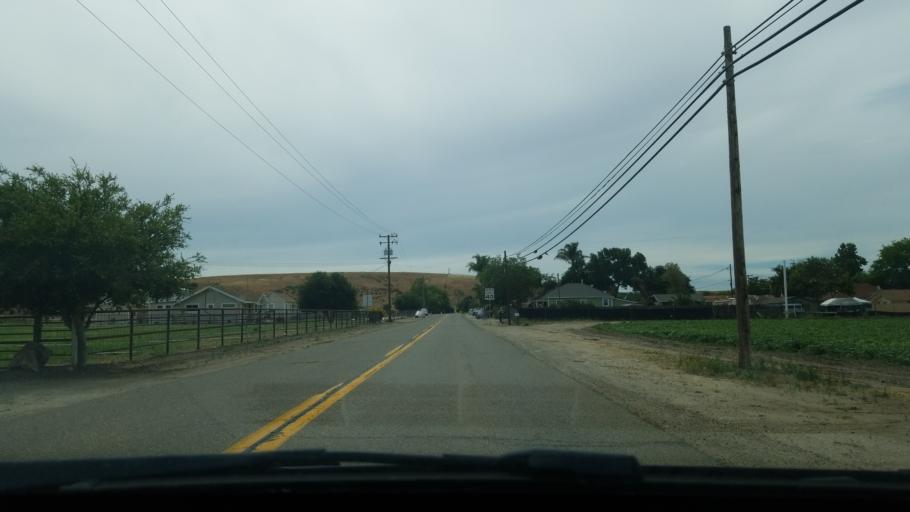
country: US
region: California
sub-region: Santa Barbara County
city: Los Alamos
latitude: 34.8646
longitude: -120.2896
